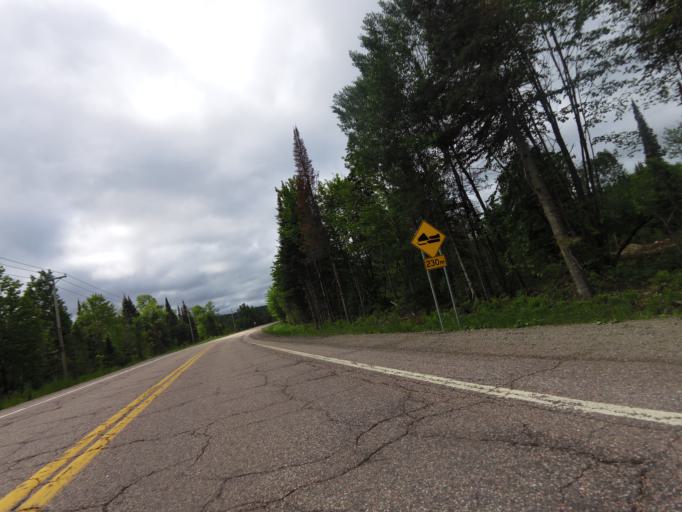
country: CA
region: Quebec
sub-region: Outaouais
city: Shawville
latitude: 45.8204
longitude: -76.4603
